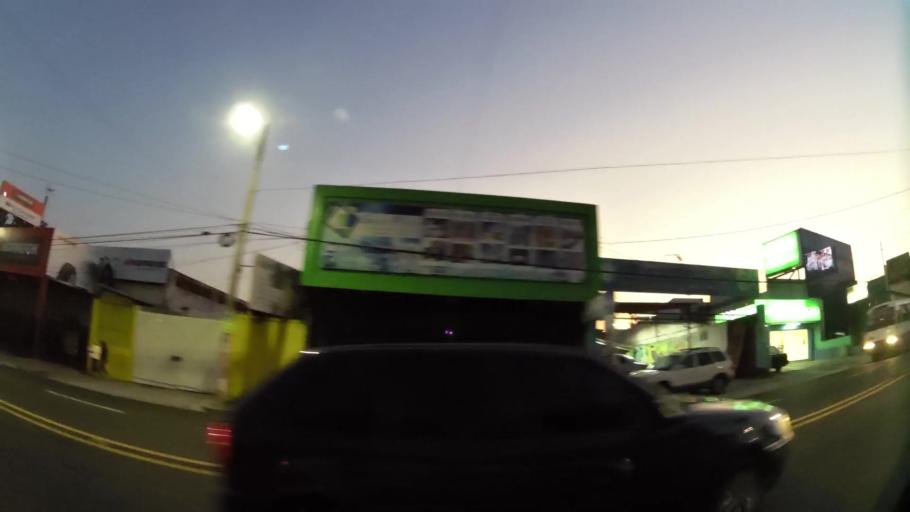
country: SV
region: La Libertad
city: Santa Tecla
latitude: 13.6797
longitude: -89.2711
